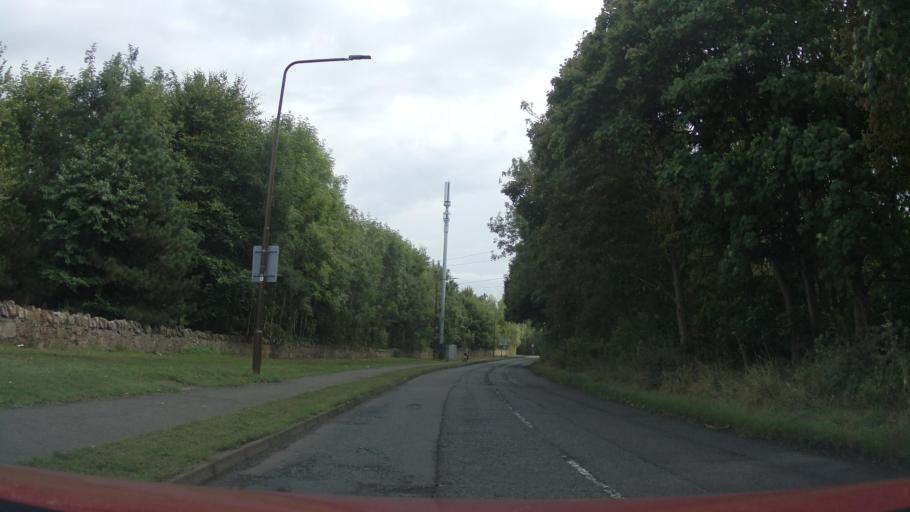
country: GB
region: Scotland
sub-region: East Lothian
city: Cockenzie
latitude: 55.9674
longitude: -2.9591
